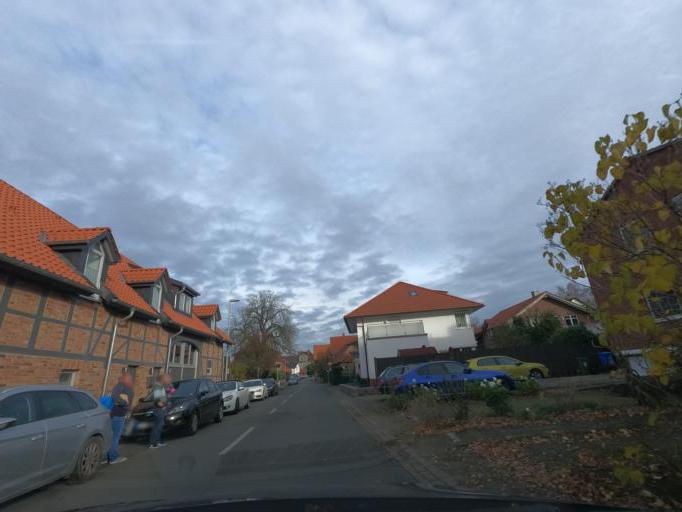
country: DE
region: Lower Saxony
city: Lehre
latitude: 52.3130
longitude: 10.6082
